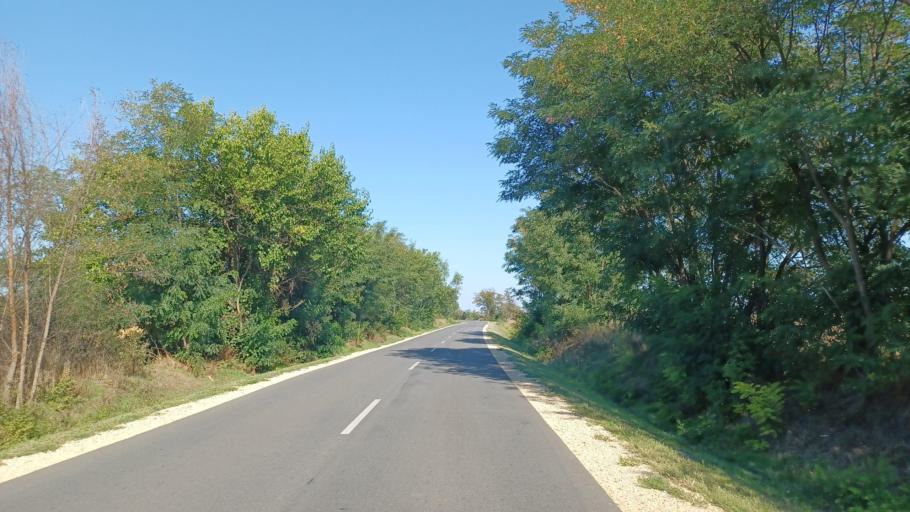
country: HU
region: Tolna
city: Nemetker
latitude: 46.6941
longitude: 18.7959
